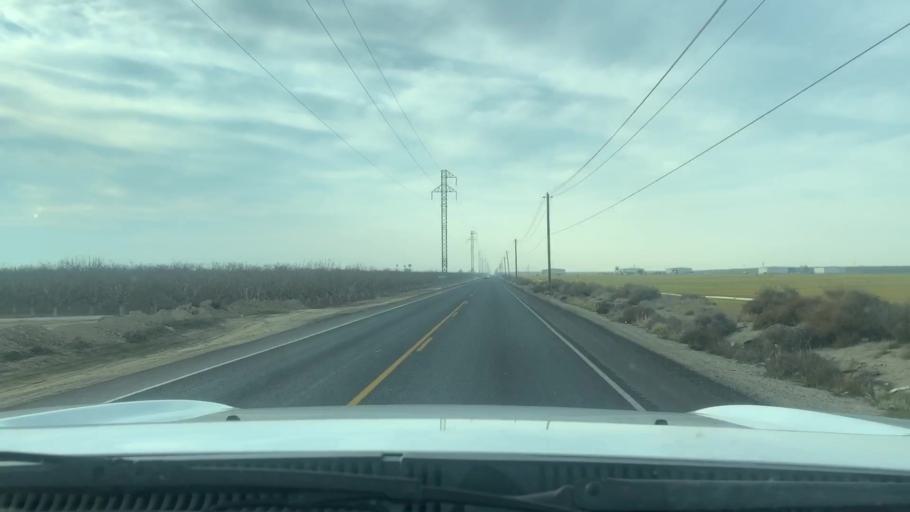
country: US
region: California
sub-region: Kern County
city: Shafter
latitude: 35.4417
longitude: -119.2702
